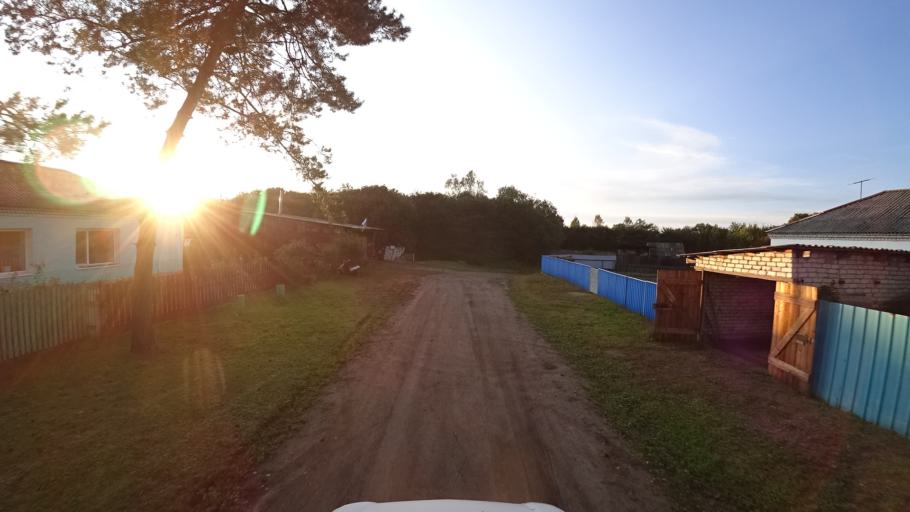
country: RU
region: Amur
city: Arkhara
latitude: 49.3614
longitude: 130.1136
